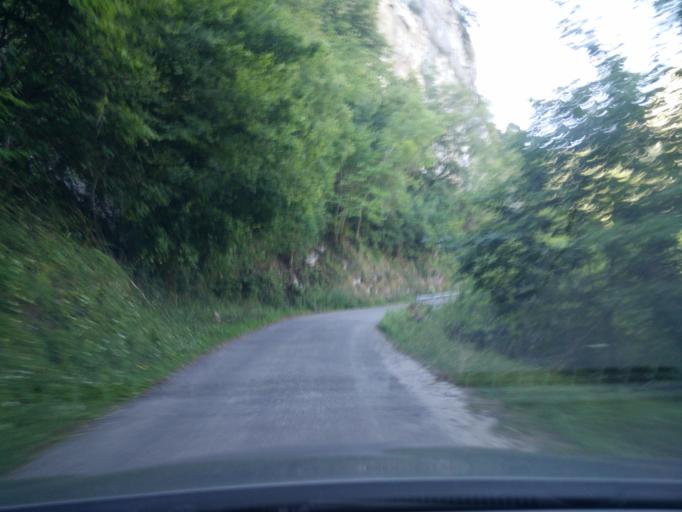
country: ES
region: Asturias
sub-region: Province of Asturias
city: Amieva
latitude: 43.1814
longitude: -5.1738
